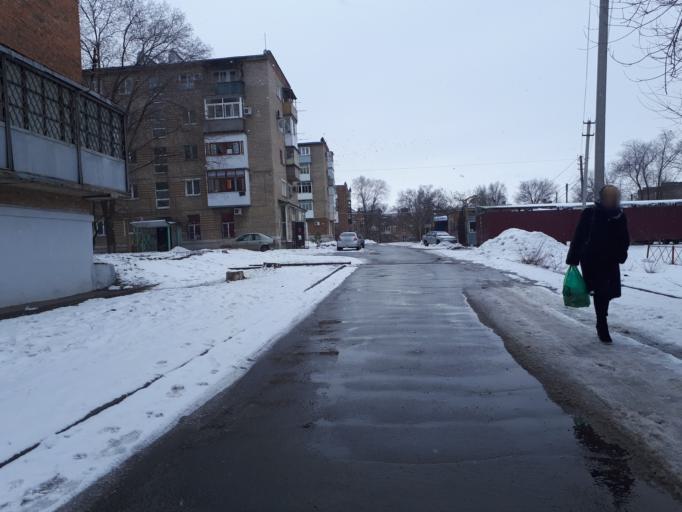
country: RU
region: Rostov
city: Krasnyy Sulin
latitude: 47.8976
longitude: 40.0615
